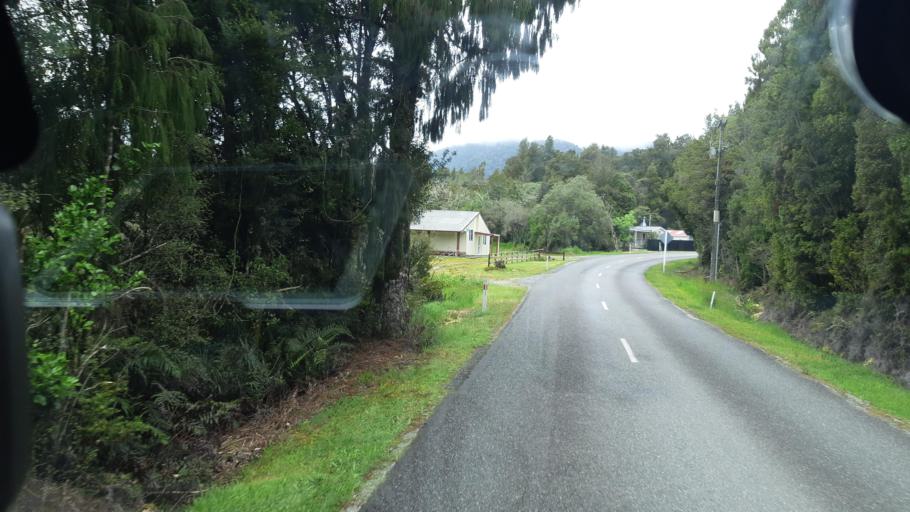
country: NZ
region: West Coast
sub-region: Westland District
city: Hokitika
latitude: -42.7957
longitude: 171.1361
